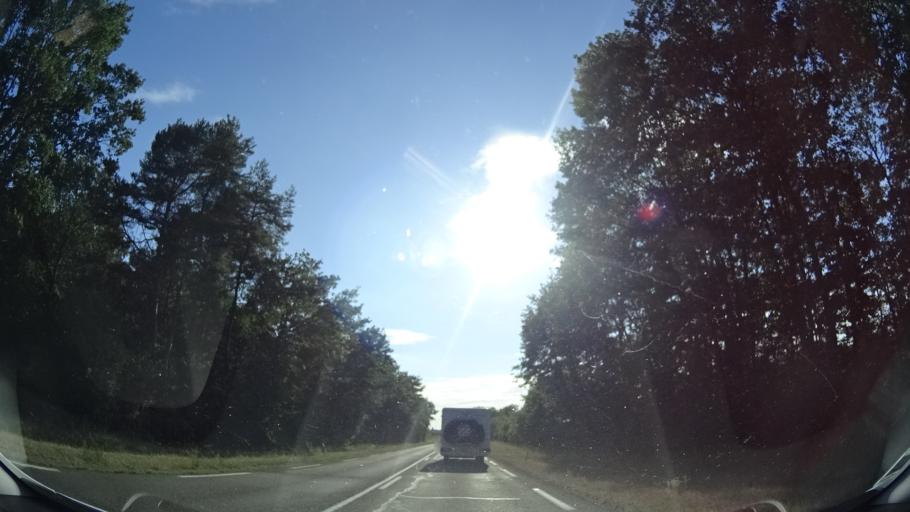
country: FR
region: Centre
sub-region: Departement du Loiret
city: Huisseau-sur-Mauves
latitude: 47.9281
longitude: 1.7332
